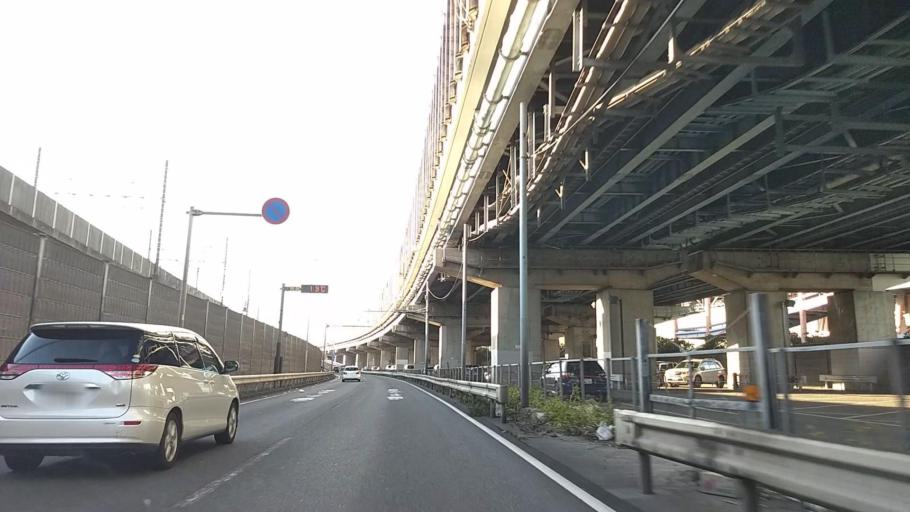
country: JP
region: Chiba
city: Funabashi
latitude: 35.6841
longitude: 139.9917
